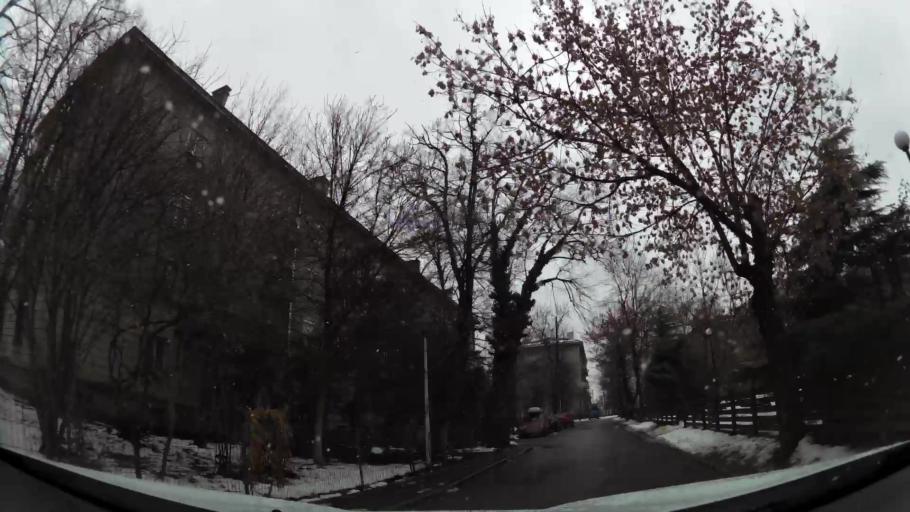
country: RO
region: Bucuresti
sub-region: Municipiul Bucuresti
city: Bucuresti
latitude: 44.4275
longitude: 26.0566
